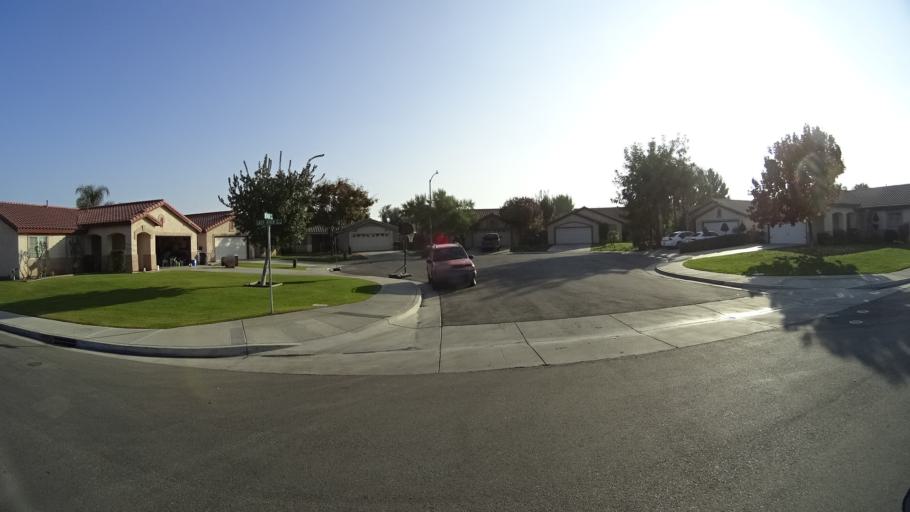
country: US
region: California
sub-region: Kern County
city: Greenfield
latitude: 35.2865
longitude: -119.0066
